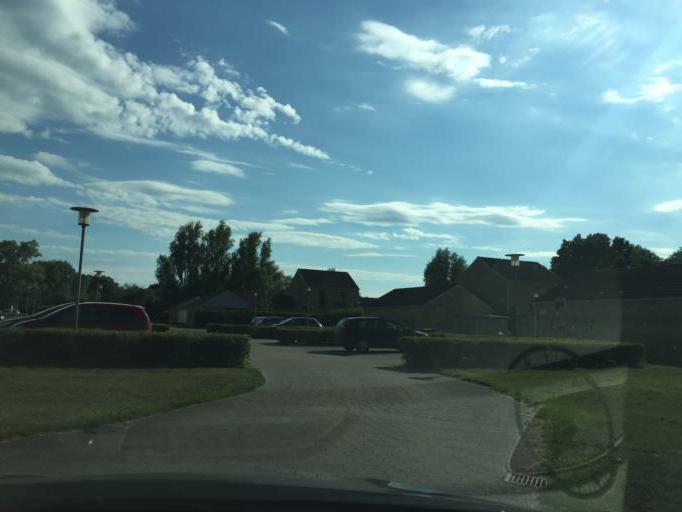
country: DK
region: South Denmark
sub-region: Odense Kommune
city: Neder Holluf
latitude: 55.3728
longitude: 10.4543
